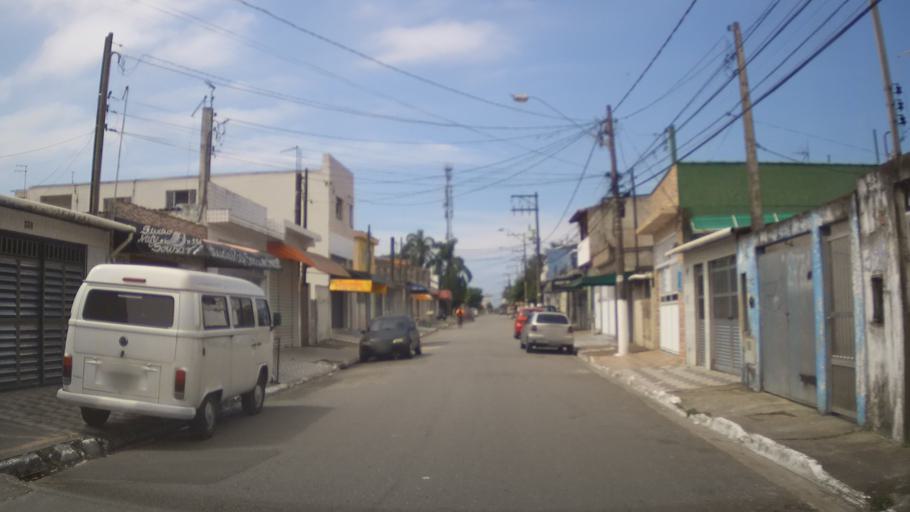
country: BR
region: Sao Paulo
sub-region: Praia Grande
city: Praia Grande
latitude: -24.0220
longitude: -46.4927
